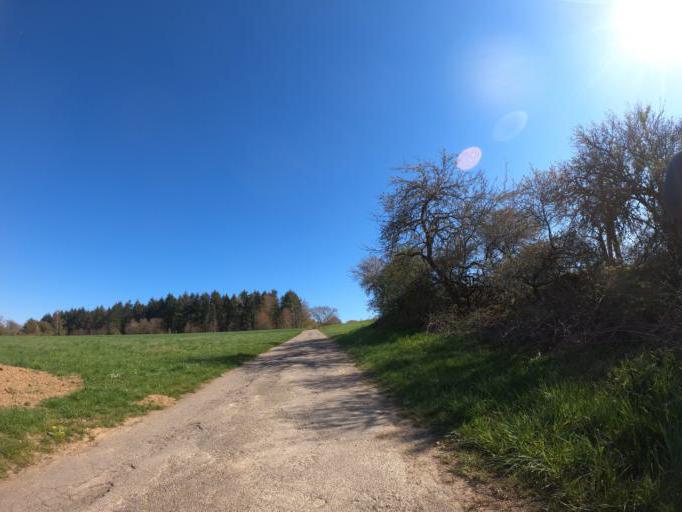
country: DE
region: Baden-Wuerttemberg
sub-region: Karlsruhe Region
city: Wiernsheim
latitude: 48.8826
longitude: 8.8596
